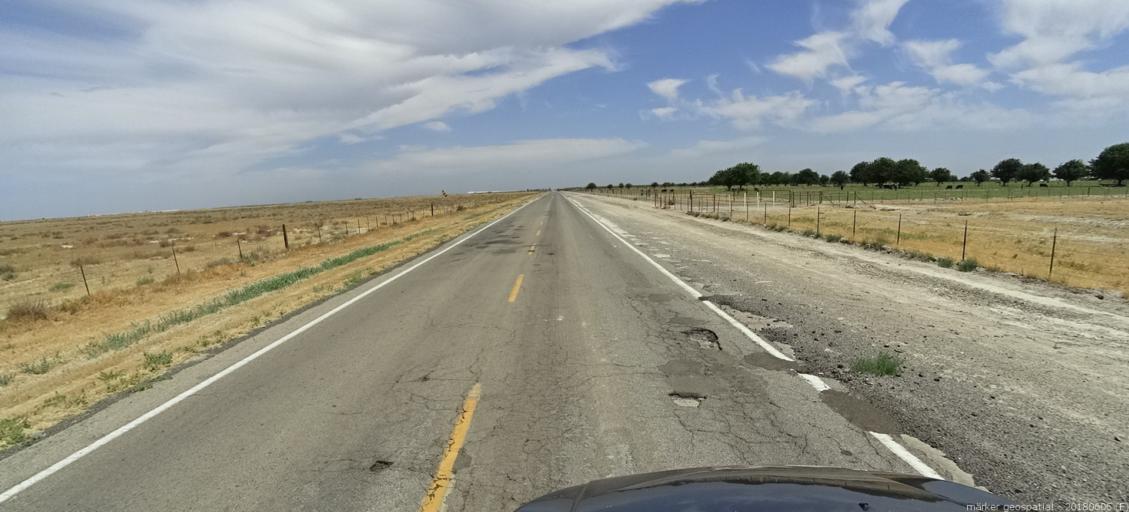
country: US
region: California
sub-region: Fresno County
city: Firebaugh
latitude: 36.9015
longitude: -120.3819
